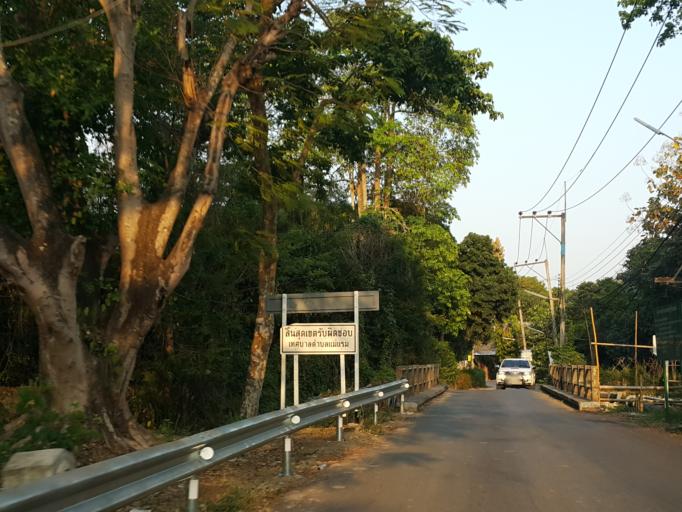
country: TH
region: Chiang Mai
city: Chiang Mai
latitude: 18.9113
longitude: 98.9256
